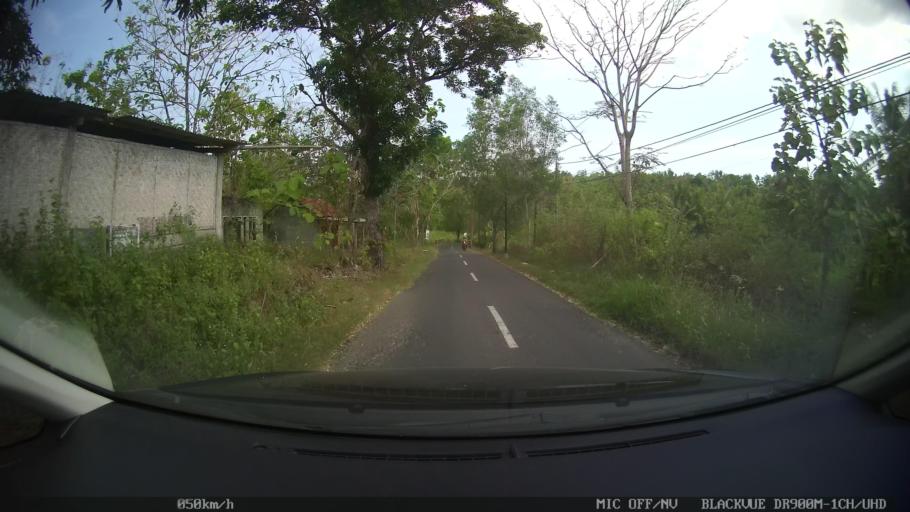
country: ID
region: Daerah Istimewa Yogyakarta
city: Bantul
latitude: -7.8583
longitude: 110.3093
